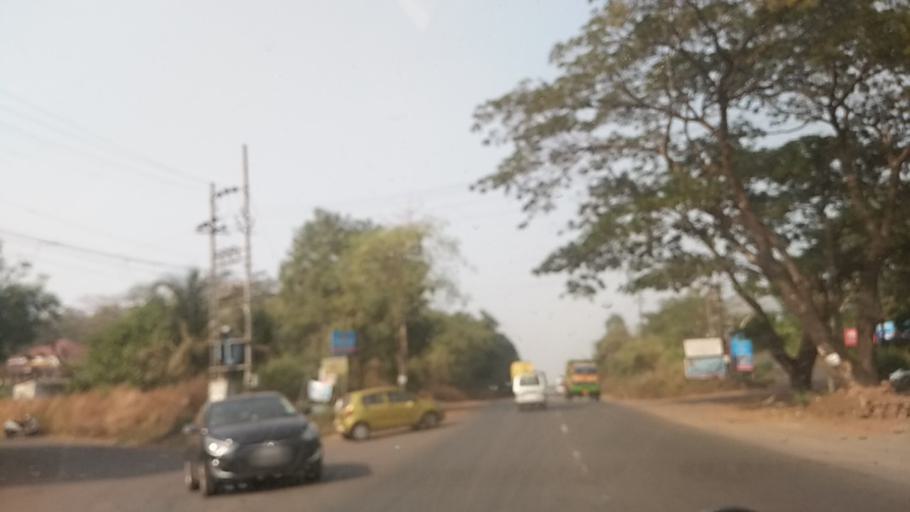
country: IN
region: Goa
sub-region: North Goa
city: Mapuca
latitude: 15.6035
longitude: 73.8247
